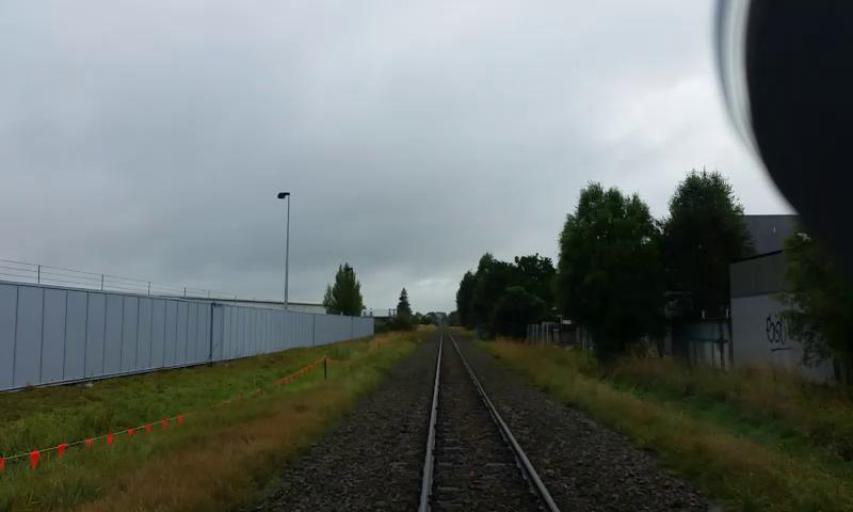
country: NZ
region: Canterbury
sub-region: Christchurch City
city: Christchurch
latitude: -43.5346
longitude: 172.6094
